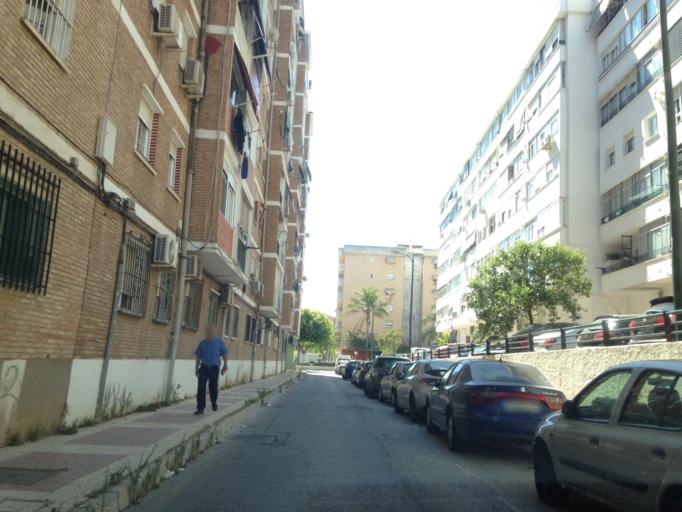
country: ES
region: Andalusia
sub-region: Provincia de Malaga
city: Malaga
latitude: 36.6965
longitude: -4.4435
